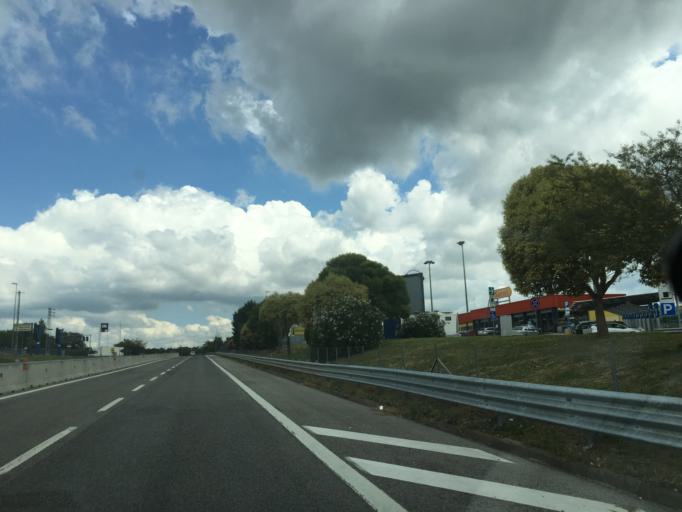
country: IT
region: Campania
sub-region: Provincia di Avellino
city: Passo di Mirabella-Pianopantano
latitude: 41.0607
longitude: 15.0128
